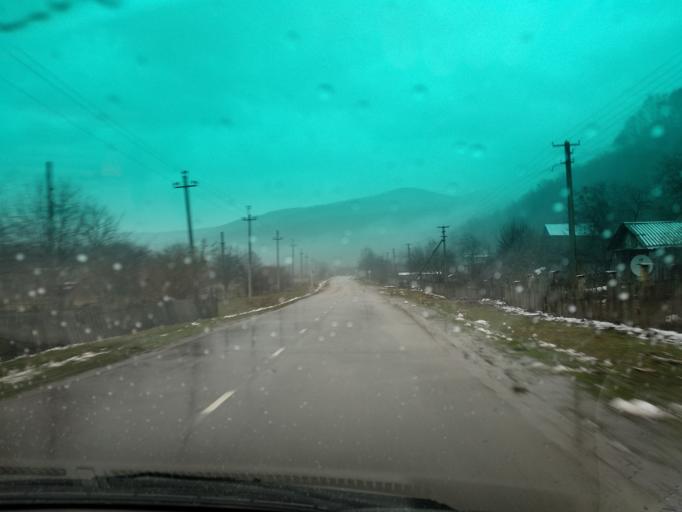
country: RU
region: Krasnodarskiy
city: Khadyzhensk
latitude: 44.2369
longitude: 39.3795
